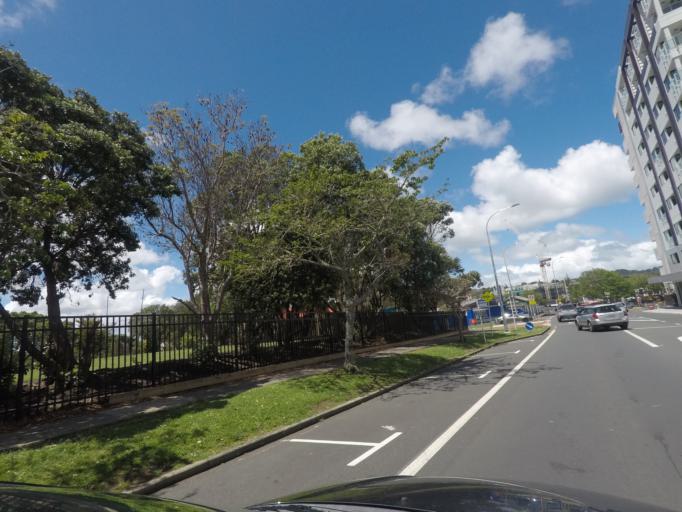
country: NZ
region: Auckland
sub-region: Auckland
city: Waitakere
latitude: -36.9091
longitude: 174.6521
